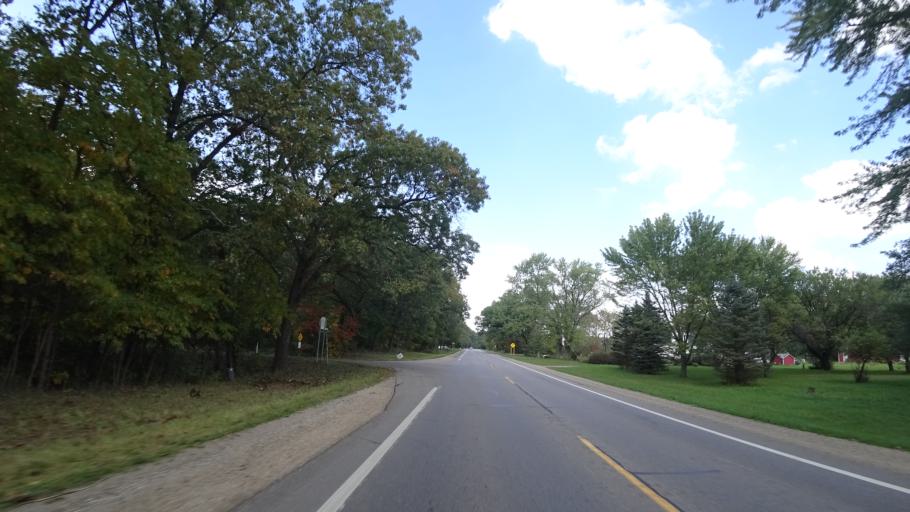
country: US
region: Michigan
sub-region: Saint Joseph County
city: Centreville
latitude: 41.9793
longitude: -85.5671
